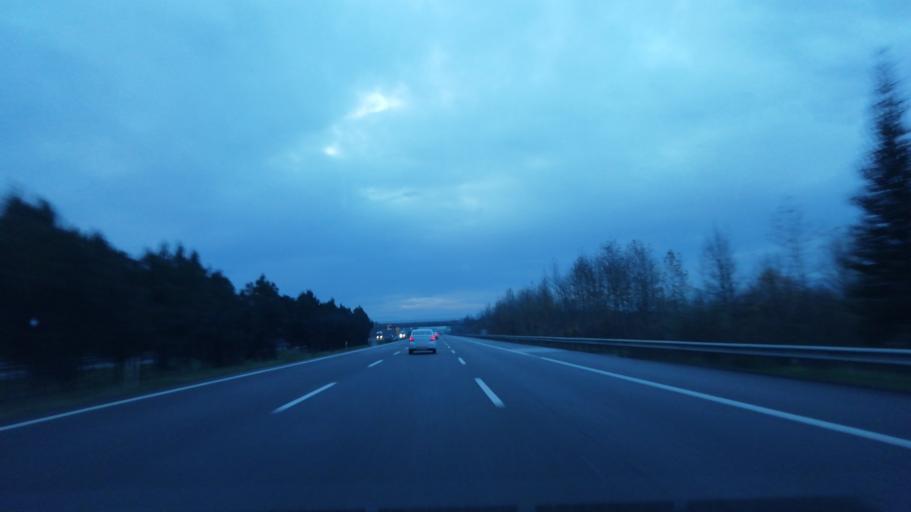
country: TR
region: Duzce
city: Duzce
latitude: 40.7971
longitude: 31.1920
